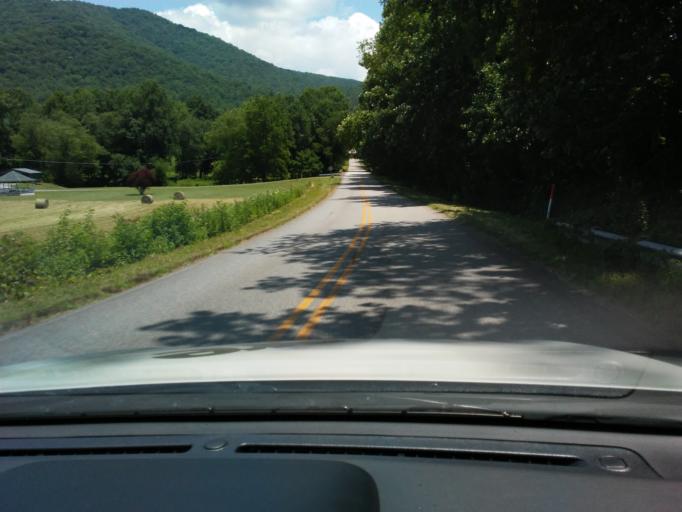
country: US
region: Georgia
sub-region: Towns County
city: Hiawassee
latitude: 34.8699
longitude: -83.7221
